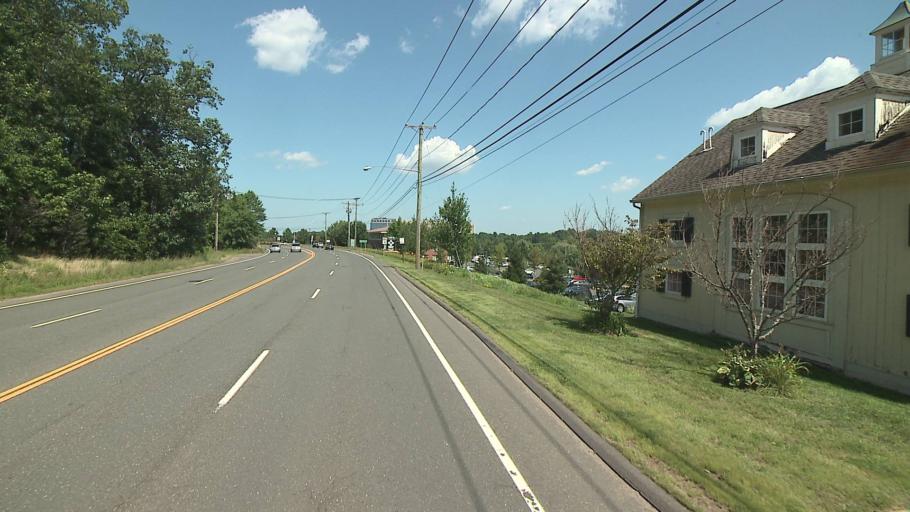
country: US
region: Connecticut
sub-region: Hartford County
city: Farmington
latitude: 41.7257
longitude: -72.8051
